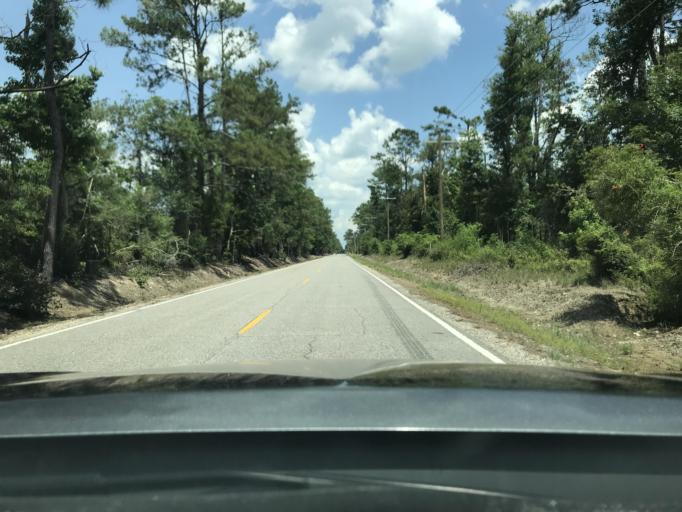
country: US
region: Louisiana
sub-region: Calcasieu Parish
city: Moss Bluff
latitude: 30.3300
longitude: -93.1561
